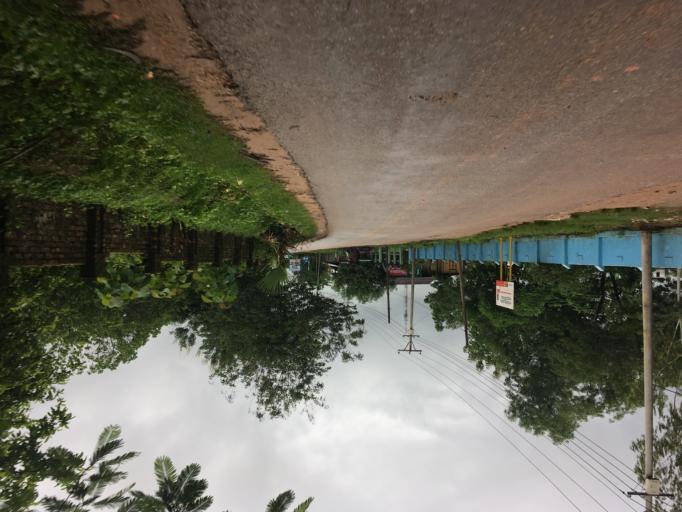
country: MM
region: Mon
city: Mudon
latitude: 16.0441
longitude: 98.1176
